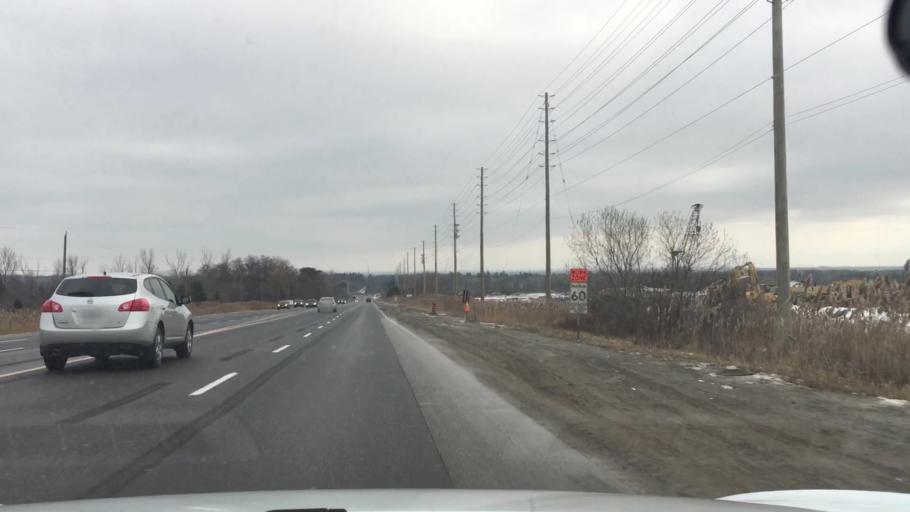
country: CA
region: Ontario
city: Pickering
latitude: 43.8789
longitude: -79.1178
